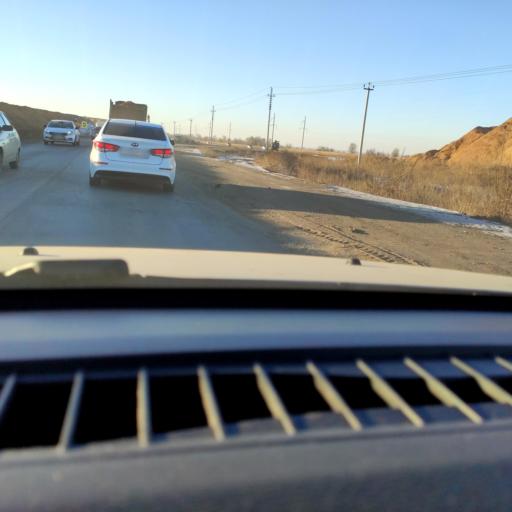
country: RU
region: Samara
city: Podstepki
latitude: 53.5611
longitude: 49.2003
